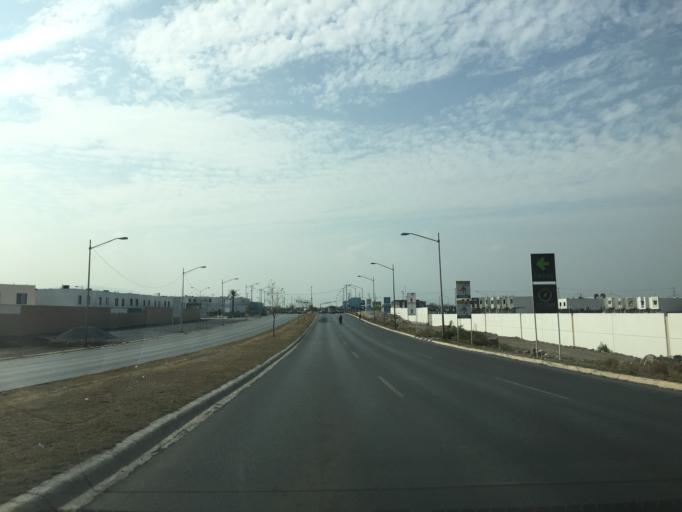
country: MX
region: Nuevo Leon
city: Apodaca
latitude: 25.7769
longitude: -100.2105
